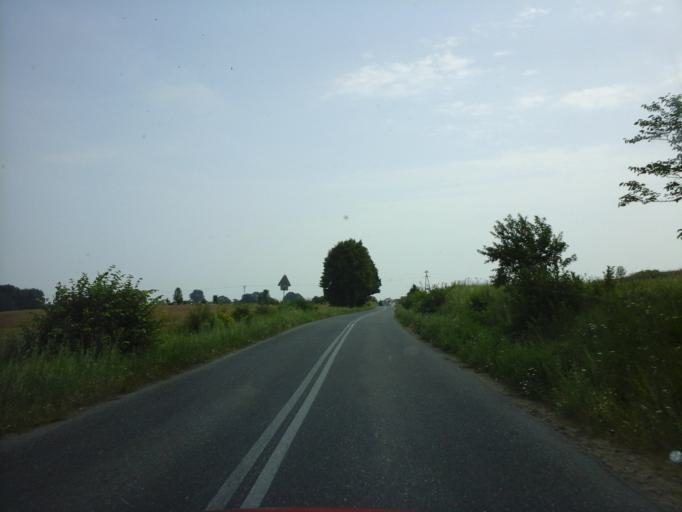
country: PL
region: West Pomeranian Voivodeship
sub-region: Powiat choszczenski
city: Pelczyce
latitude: 53.0551
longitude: 15.3209
